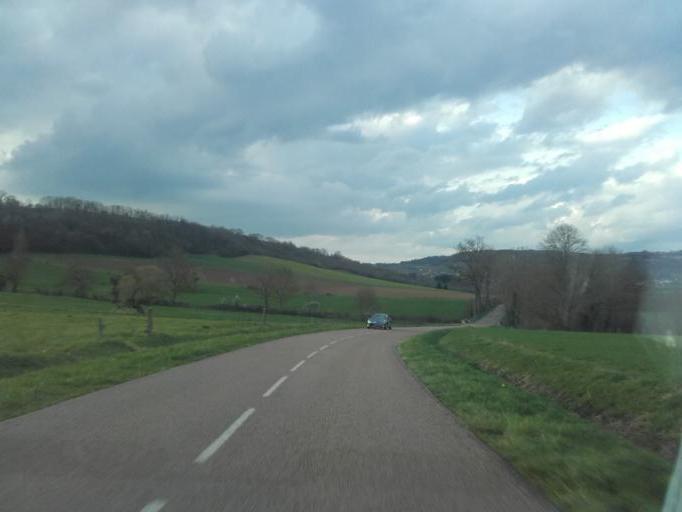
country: FR
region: Bourgogne
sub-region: Departement de la Cote-d'Or
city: Nolay
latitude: 46.9393
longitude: 4.6225
